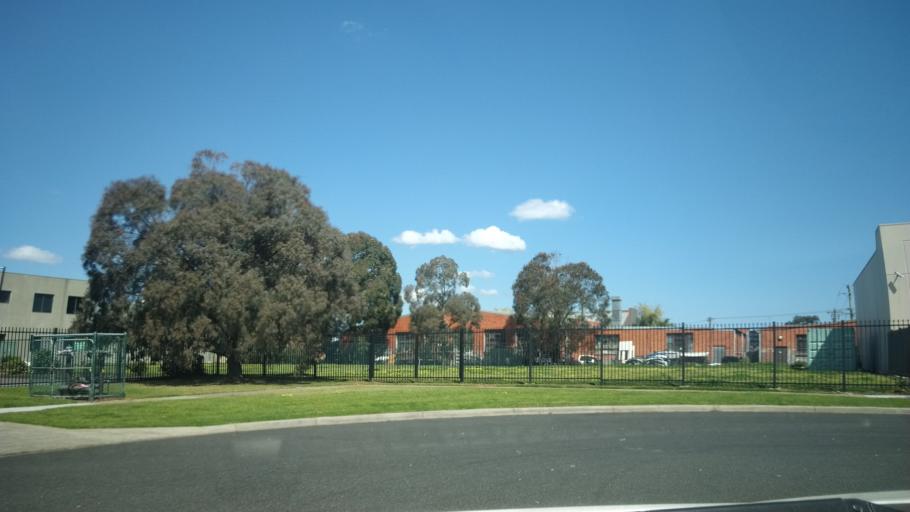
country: AU
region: Victoria
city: Highett
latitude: -37.9443
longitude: 145.0560
